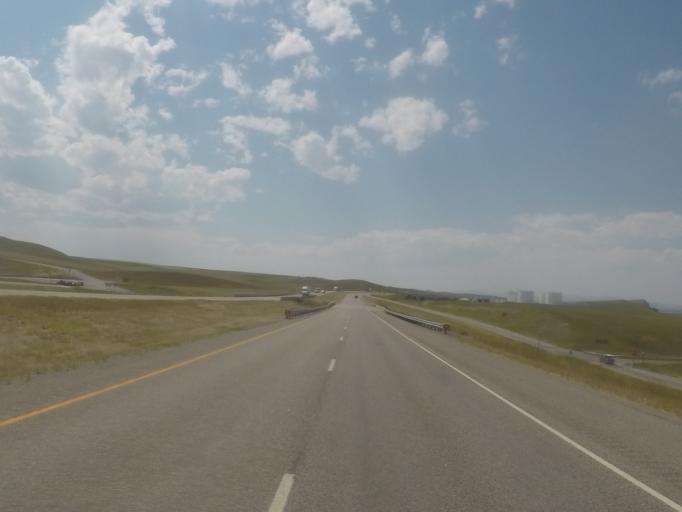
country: US
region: Montana
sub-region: Gallatin County
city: Manhattan
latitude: 45.8820
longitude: -111.4359
